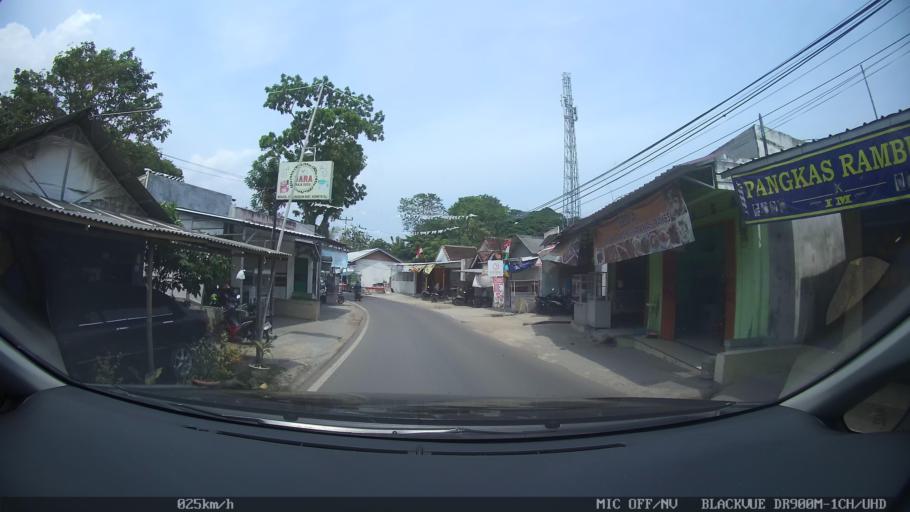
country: ID
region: Lampung
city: Bandarlampung
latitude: -5.4525
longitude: 105.2525
